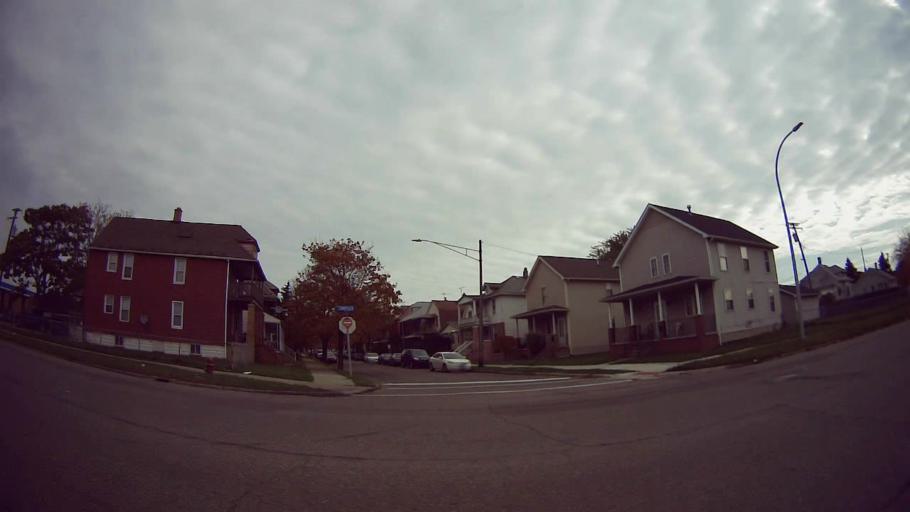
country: US
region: Michigan
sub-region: Wayne County
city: Hamtramck
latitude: 42.3963
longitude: -83.0679
